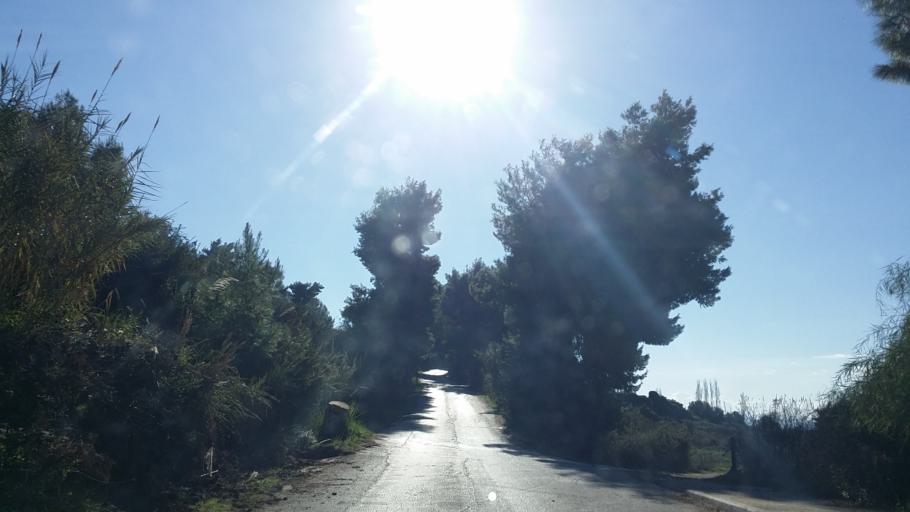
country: GR
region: West Greece
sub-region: Nomos Aitolias kai Akarnanias
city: Palairos
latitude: 38.7758
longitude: 20.8811
